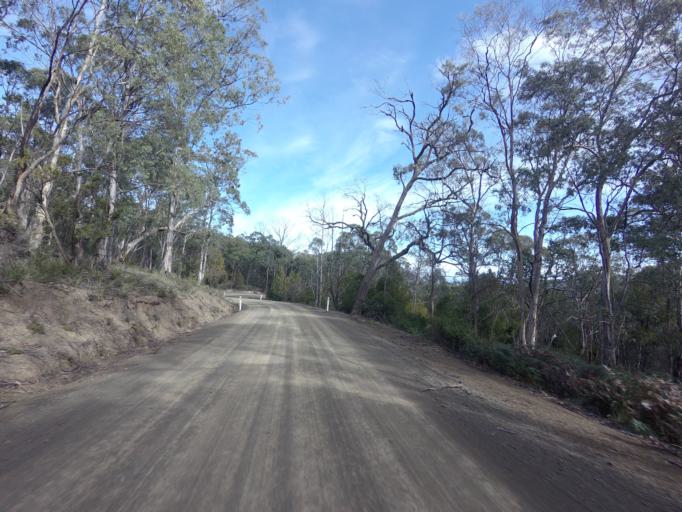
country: AU
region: Tasmania
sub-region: Clarence
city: Sandford
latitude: -43.0888
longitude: 147.7042
